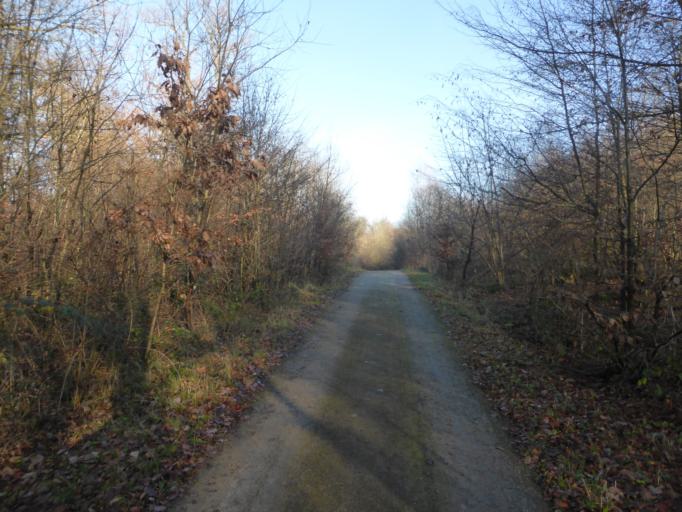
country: LU
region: Luxembourg
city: Hautcharage
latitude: 49.5859
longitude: 5.8996
